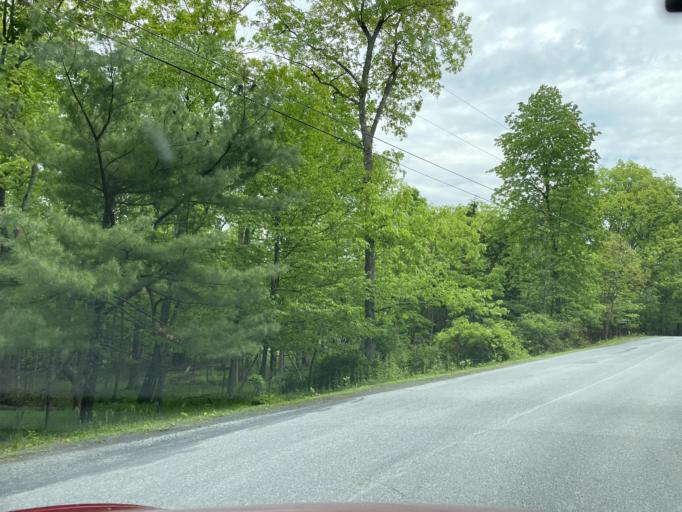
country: US
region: New York
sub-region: Ulster County
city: Woodstock
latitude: 42.0320
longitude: -74.1199
